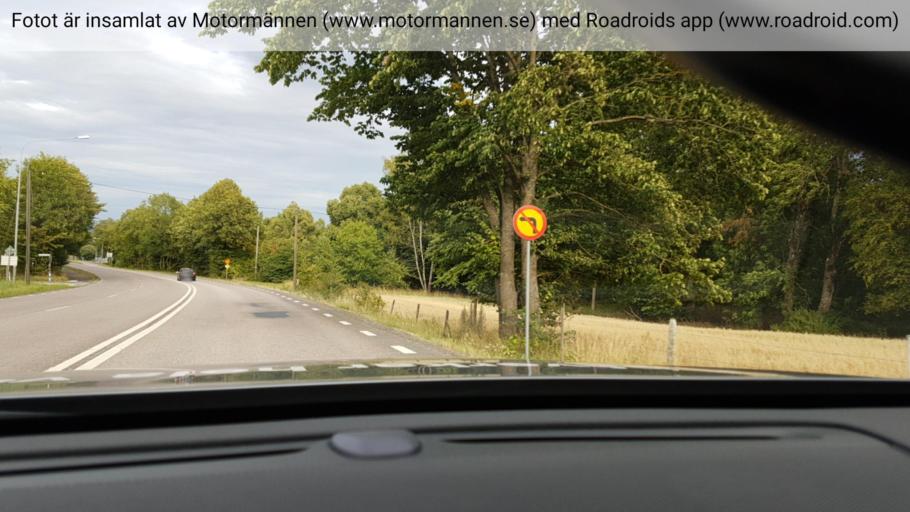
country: SE
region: Vaestra Goetaland
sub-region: Skovde Kommun
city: Skoevde
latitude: 58.3806
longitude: 13.8171
